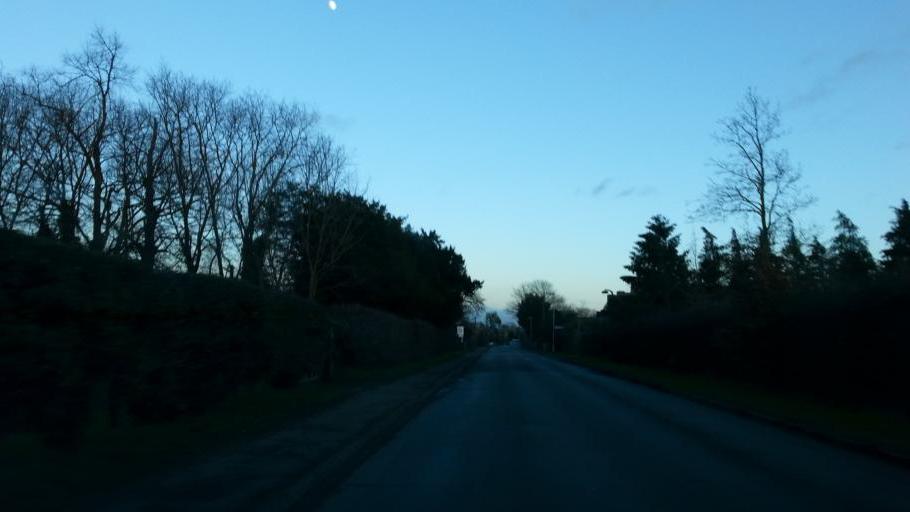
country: GB
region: England
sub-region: Cambridgeshire
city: Needingworth
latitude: 52.2983
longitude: -0.0445
